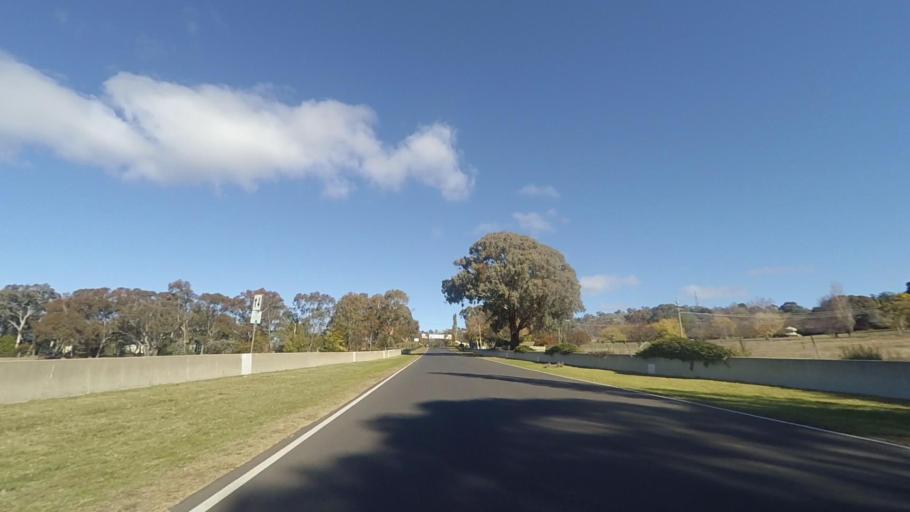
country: AU
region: New South Wales
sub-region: Bathurst Regional
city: Bathurst
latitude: -33.4433
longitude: 149.5548
